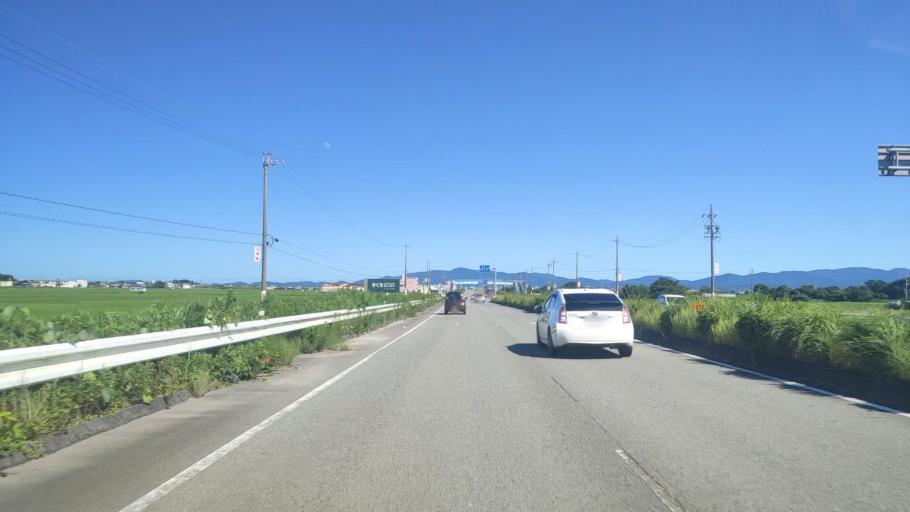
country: JP
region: Mie
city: Ise
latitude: 34.5615
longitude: 136.6433
